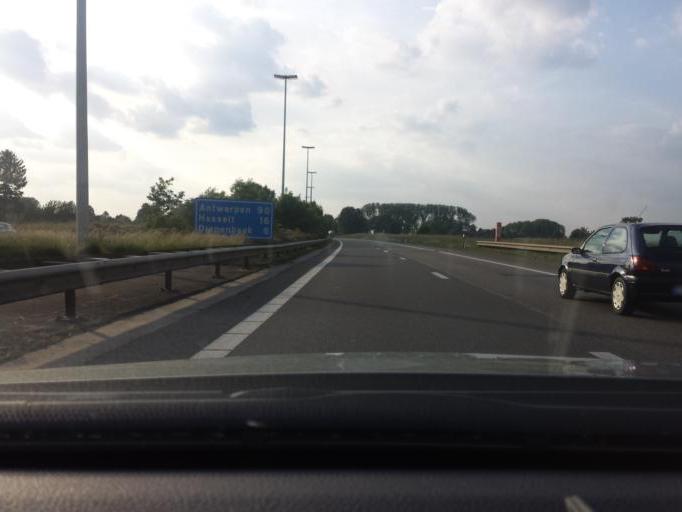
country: BE
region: Flanders
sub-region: Provincie Limburg
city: Hoeselt
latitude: 50.8661
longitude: 5.4940
